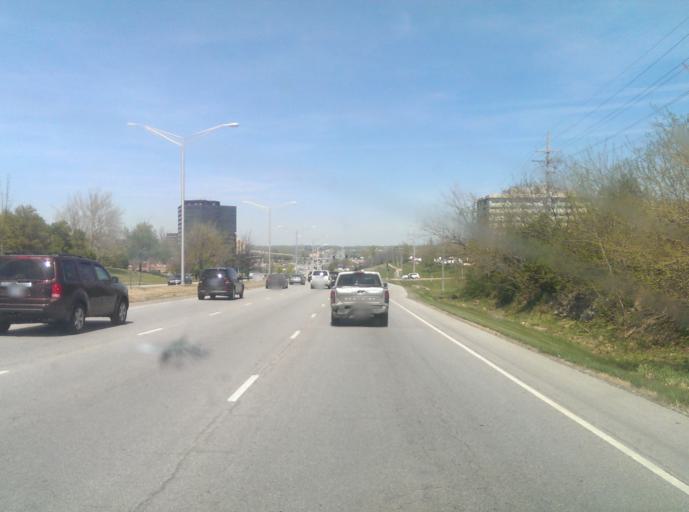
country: US
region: Kansas
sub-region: Johnson County
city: Overland Park
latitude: 38.9205
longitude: -94.6674
